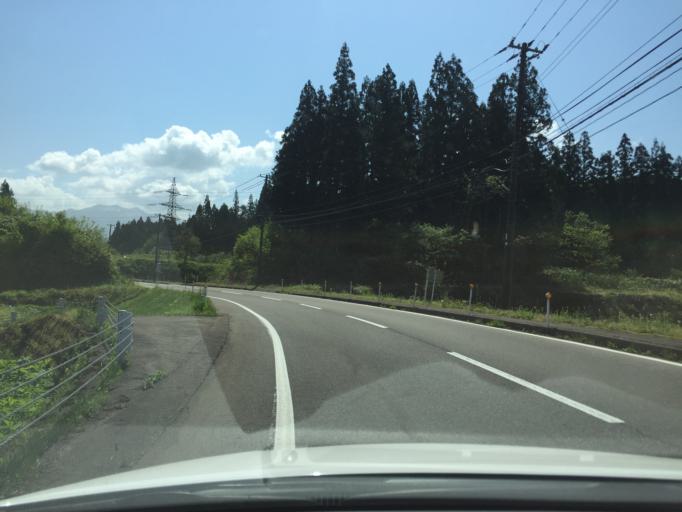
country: JP
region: Niigata
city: Kamo
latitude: 37.5773
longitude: 139.0741
